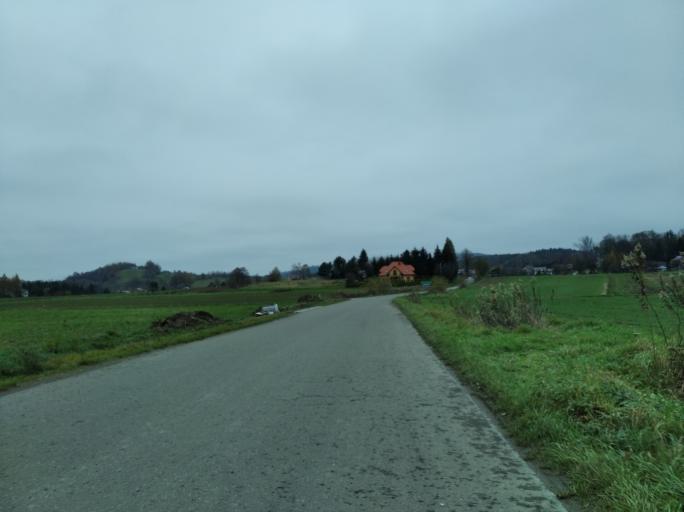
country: PL
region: Subcarpathian Voivodeship
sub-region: Powiat krosnienski
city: Leki
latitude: 49.7992
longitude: 21.6685
